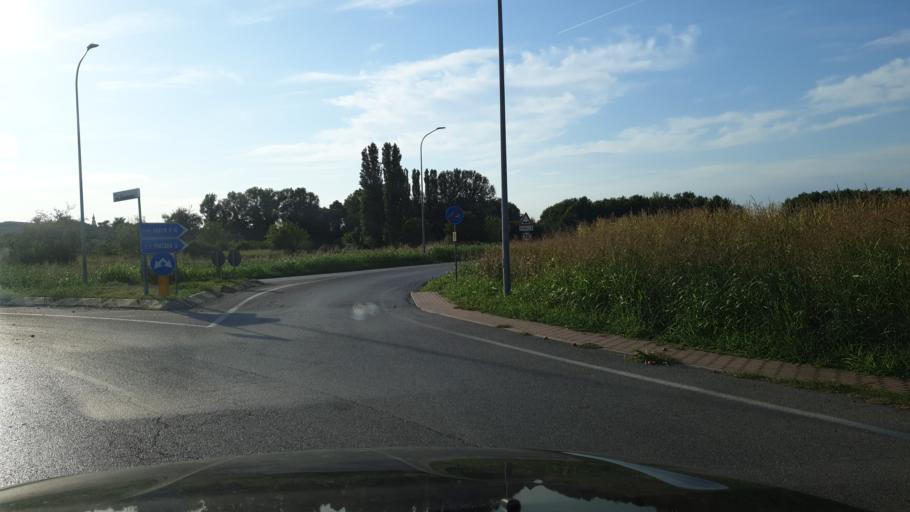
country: IT
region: Veneto
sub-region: Provincia di Rovigo
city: Fiesso Umbertiano
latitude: 44.9609
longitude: 11.6159
